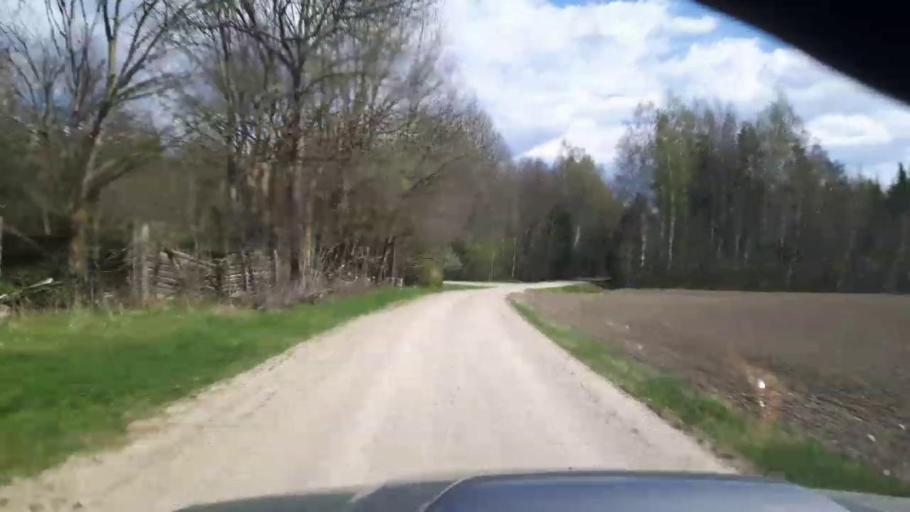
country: EE
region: Paernumaa
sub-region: Tootsi vald
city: Tootsi
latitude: 58.4545
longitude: 24.8172
